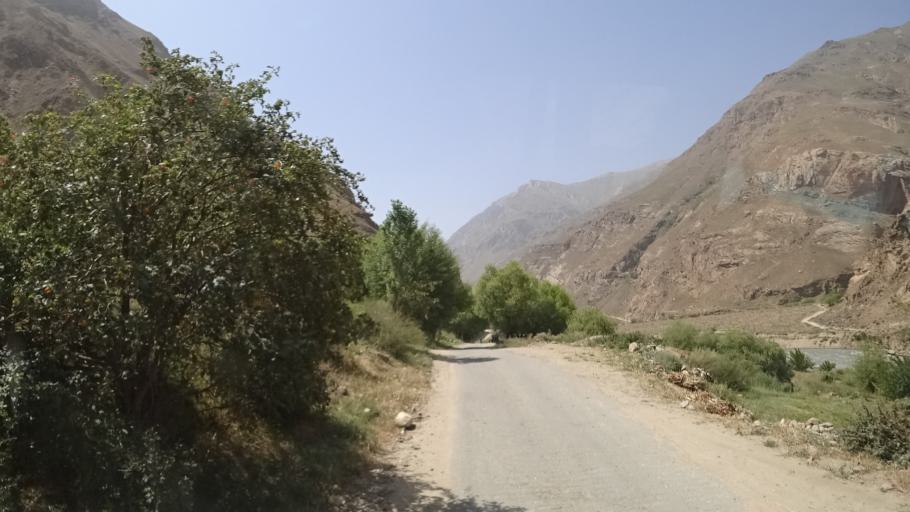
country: TJ
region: Gorno-Badakhshan
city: Khorugh
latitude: 37.1498
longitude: 71.4506
